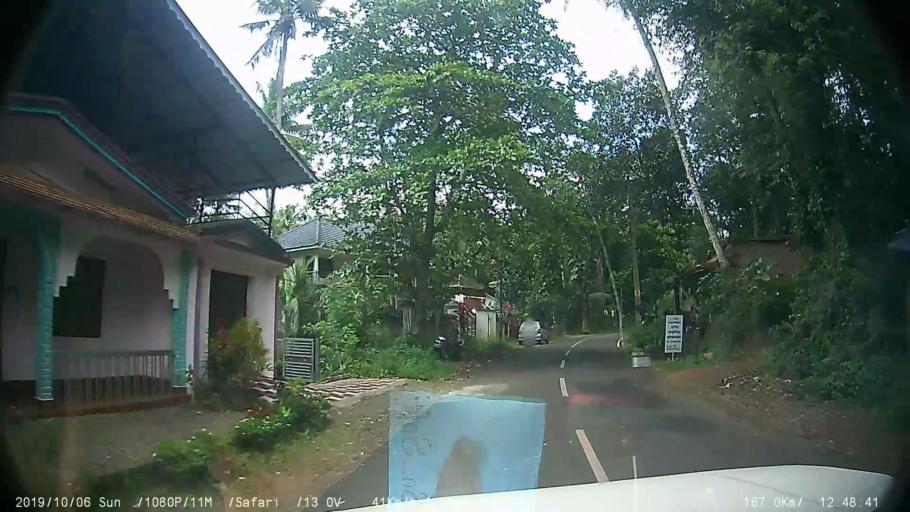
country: IN
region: Kerala
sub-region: Kottayam
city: Palackattumala
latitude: 9.7811
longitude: 76.5973
